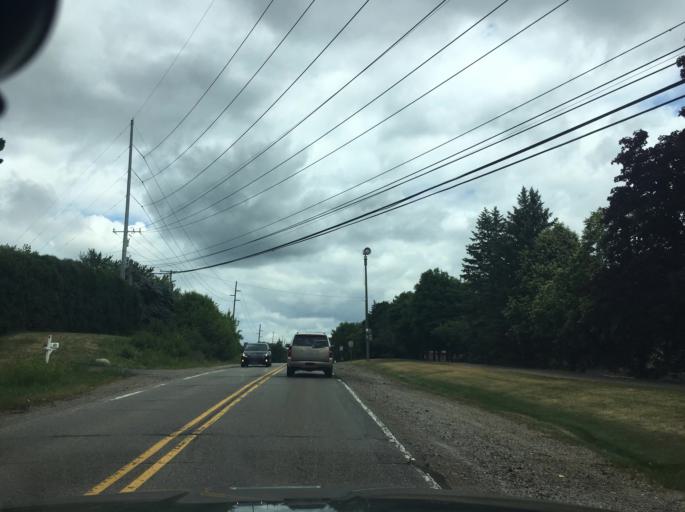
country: US
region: Michigan
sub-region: Oakland County
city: Rochester
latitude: 42.6876
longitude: -83.1536
